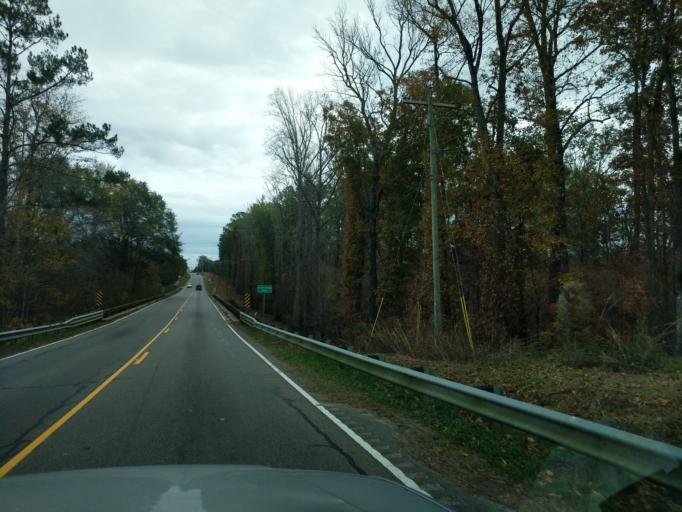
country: US
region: South Carolina
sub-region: Saluda County
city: Saluda
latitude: 33.9956
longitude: -81.7635
